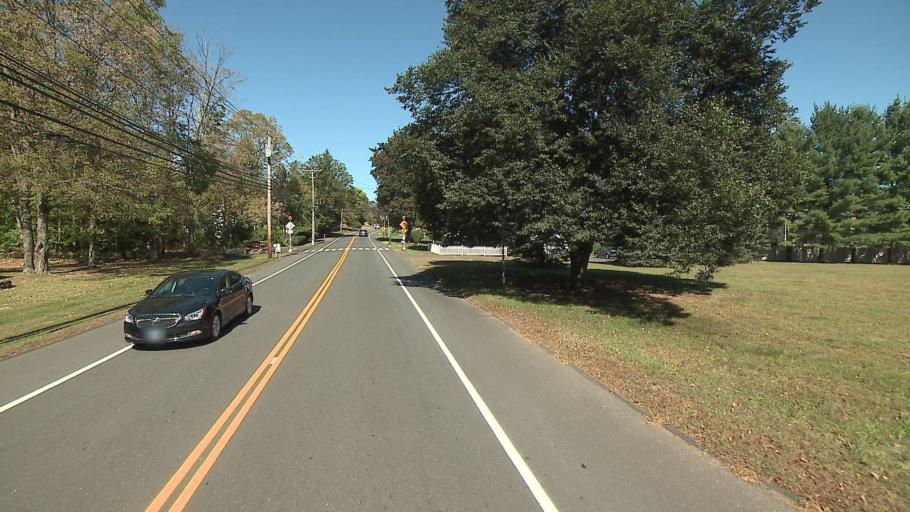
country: US
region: Connecticut
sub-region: Hartford County
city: Salmon Brook
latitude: 41.9466
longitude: -72.7908
